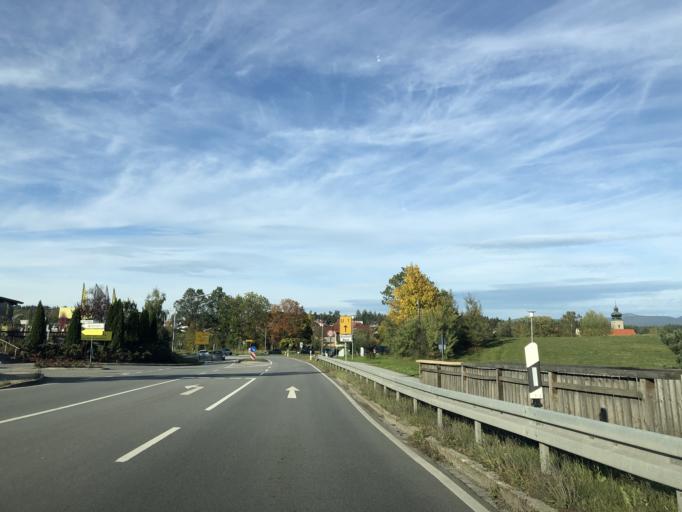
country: DE
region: Bavaria
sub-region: Lower Bavaria
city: Patersdorf
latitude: 49.0113
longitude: 12.9829
